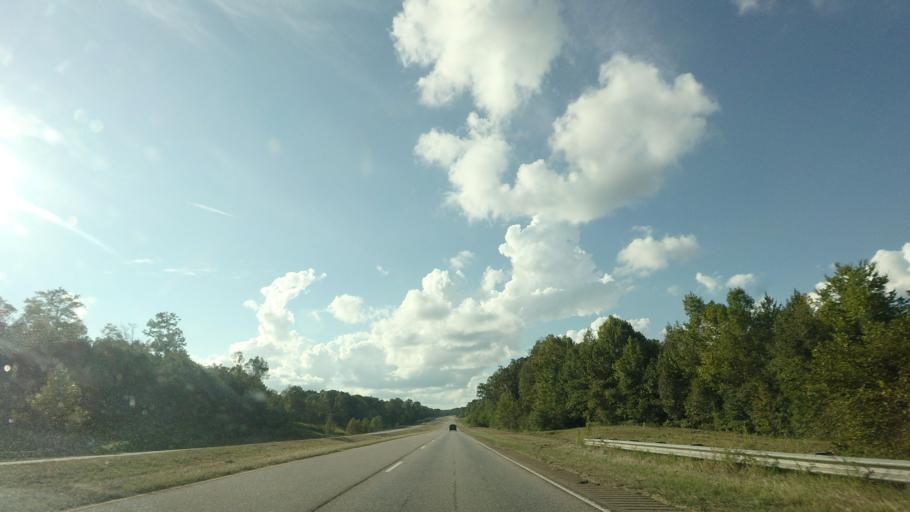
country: US
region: Georgia
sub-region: Pulaski County
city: Hawkinsville
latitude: 32.3623
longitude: -83.6011
